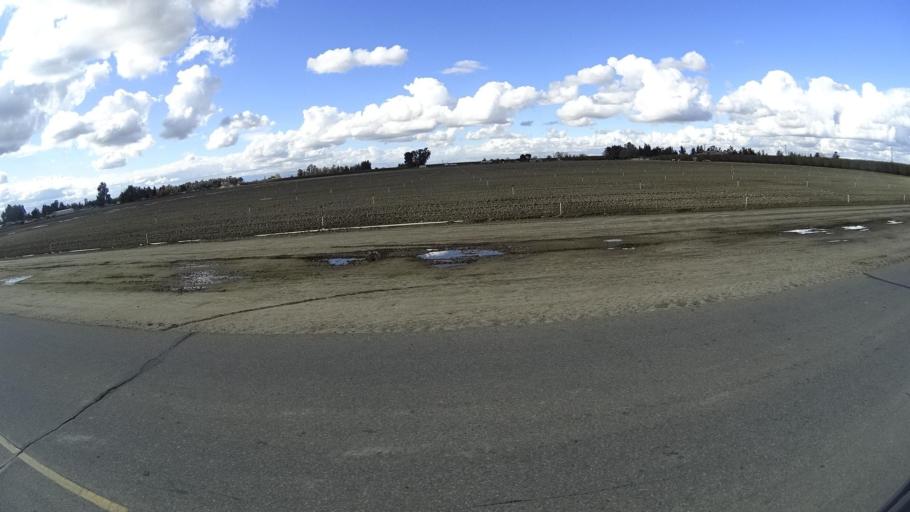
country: US
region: California
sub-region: Kern County
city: Greenfield
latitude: 35.2434
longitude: -119.0744
